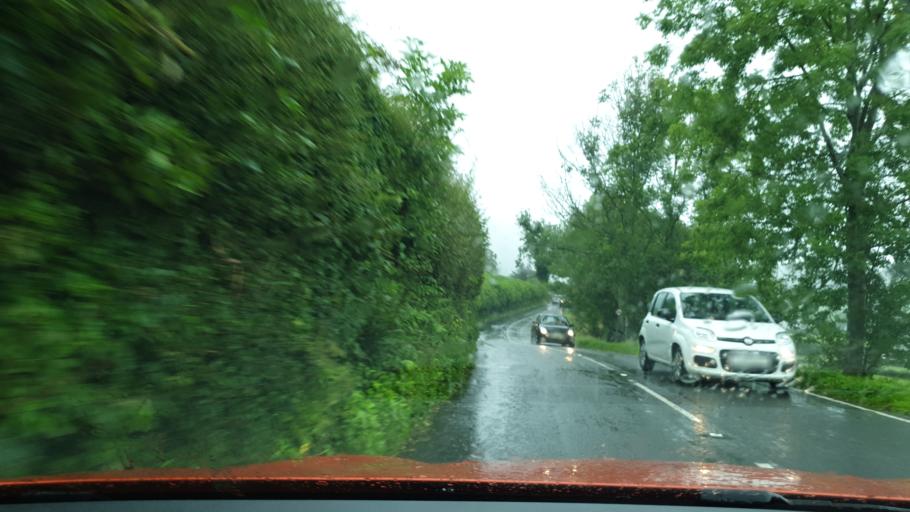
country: GB
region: England
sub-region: Cumbria
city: Ambleside
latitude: 54.3629
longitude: -3.0781
